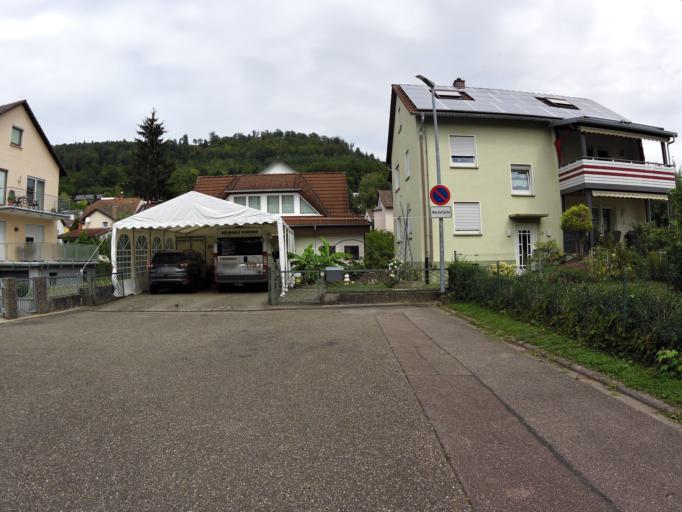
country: DE
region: Baden-Wuerttemberg
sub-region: Freiburg Region
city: Hohberg
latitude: 48.3390
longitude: 7.9034
